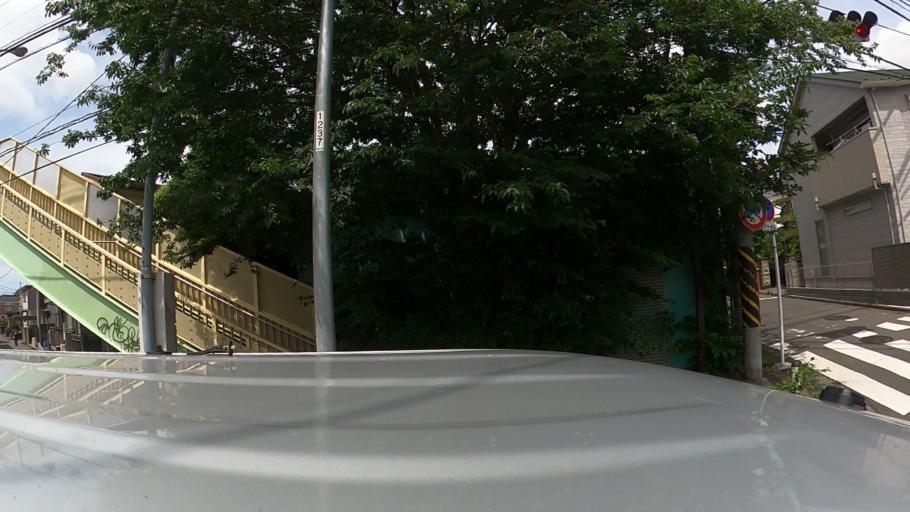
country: JP
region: Kanagawa
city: Fujisawa
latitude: 35.4091
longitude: 139.4698
